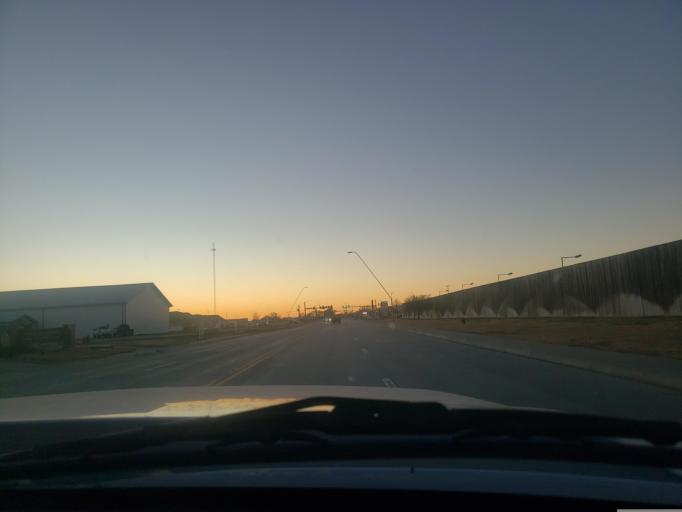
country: US
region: Kansas
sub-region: Finney County
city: Garden City
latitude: 37.9748
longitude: -100.8338
